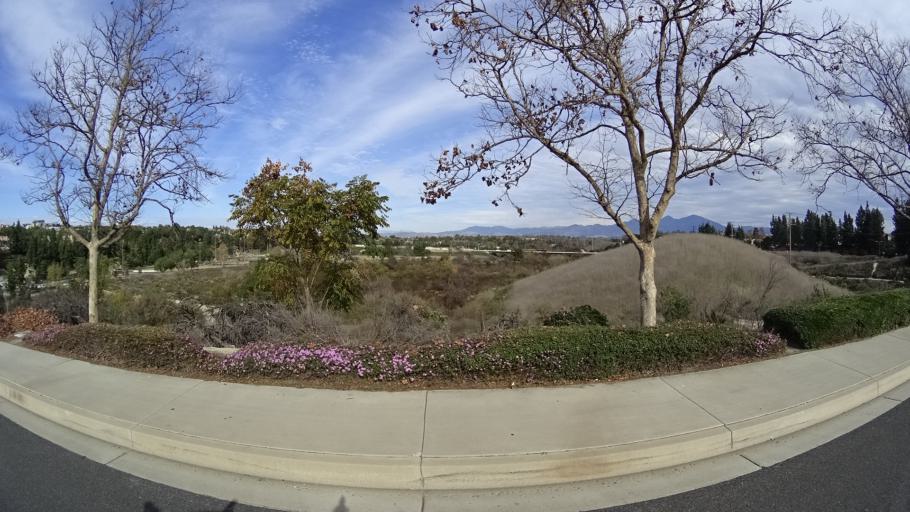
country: US
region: California
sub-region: Orange County
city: Aliso Viejo
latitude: 33.5718
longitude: -117.7157
